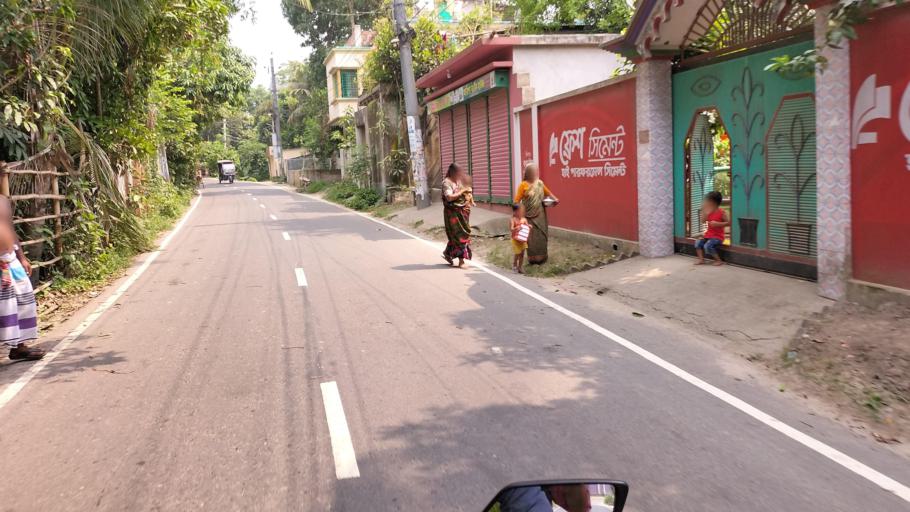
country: BD
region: Dhaka
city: Azimpur
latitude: 23.7009
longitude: 90.2918
